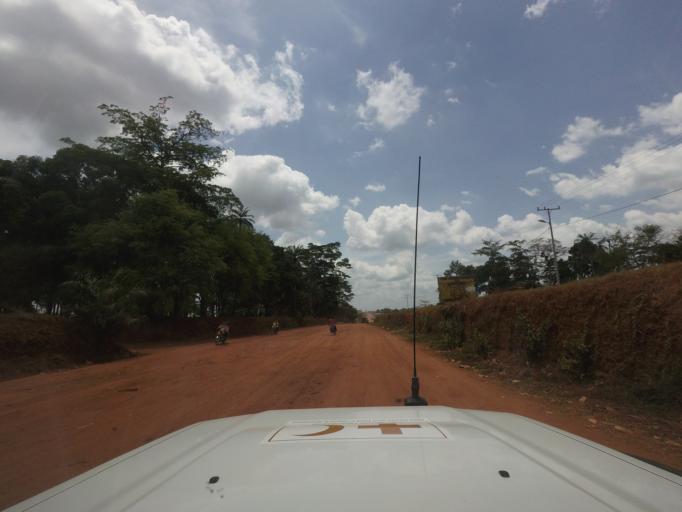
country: LR
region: Nimba
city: Sanniquellie
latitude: 7.2345
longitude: -8.9769
